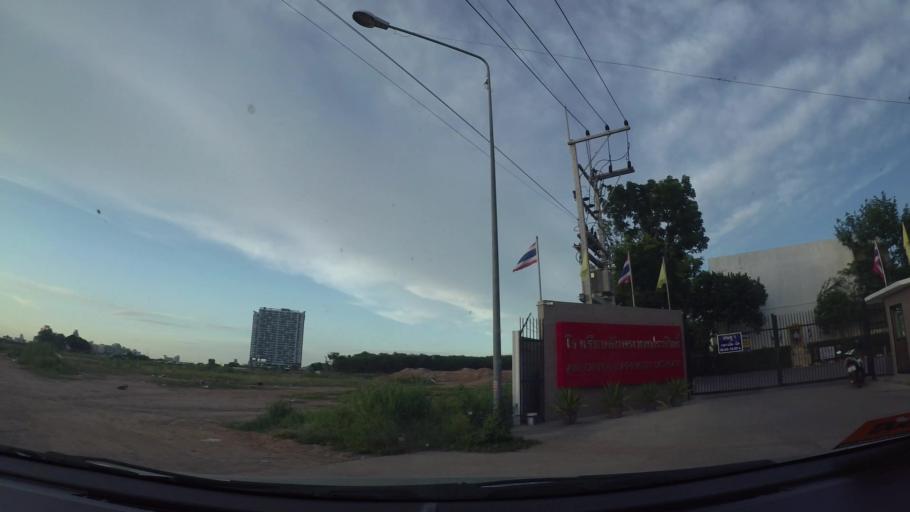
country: TH
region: Chon Buri
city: Phatthaya
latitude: 12.9117
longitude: 100.8892
